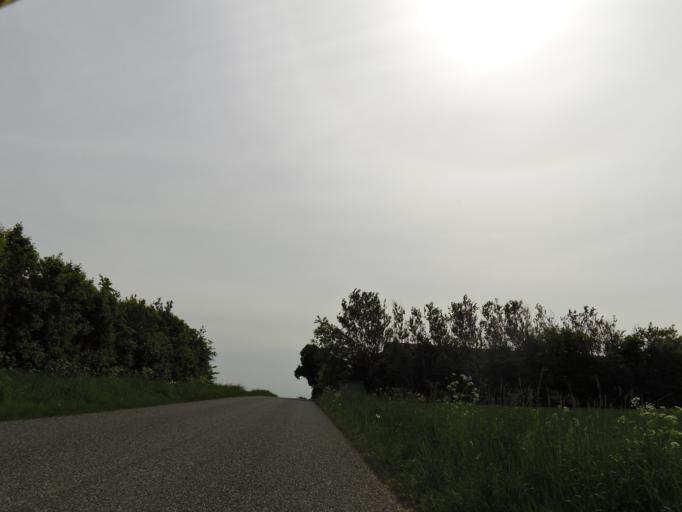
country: DK
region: Central Jutland
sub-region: Holstebro Kommune
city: Vinderup
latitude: 56.5784
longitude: 8.7709
